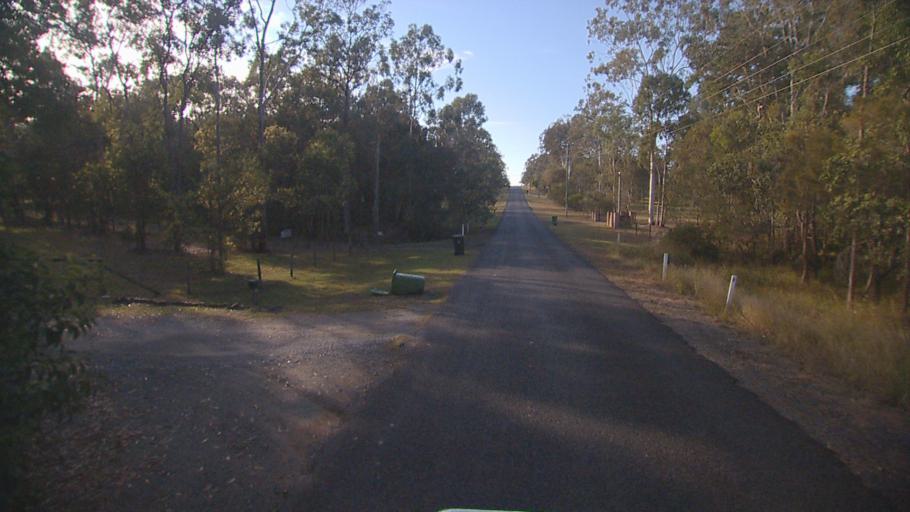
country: AU
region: Queensland
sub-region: Logan
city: North Maclean
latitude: -27.7560
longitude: 152.9992
